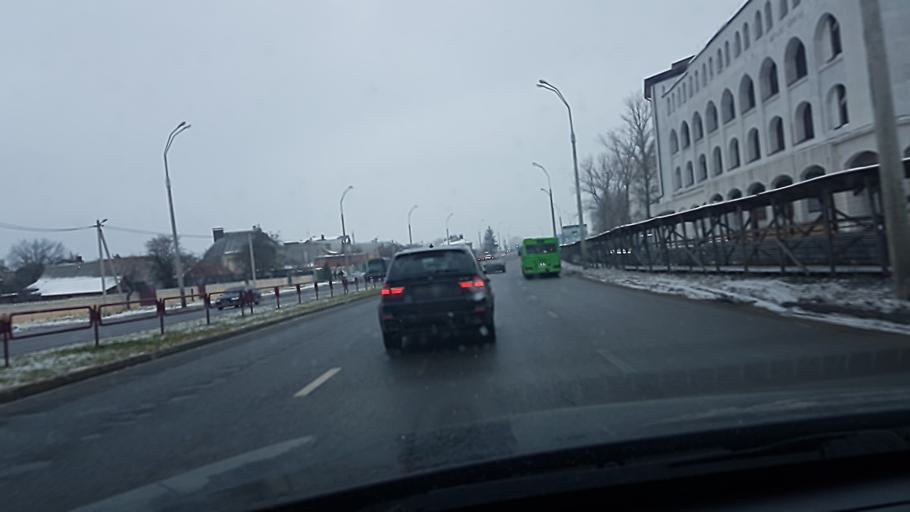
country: BY
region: Minsk
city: Bal'shavik
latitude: 53.9555
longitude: 27.5353
